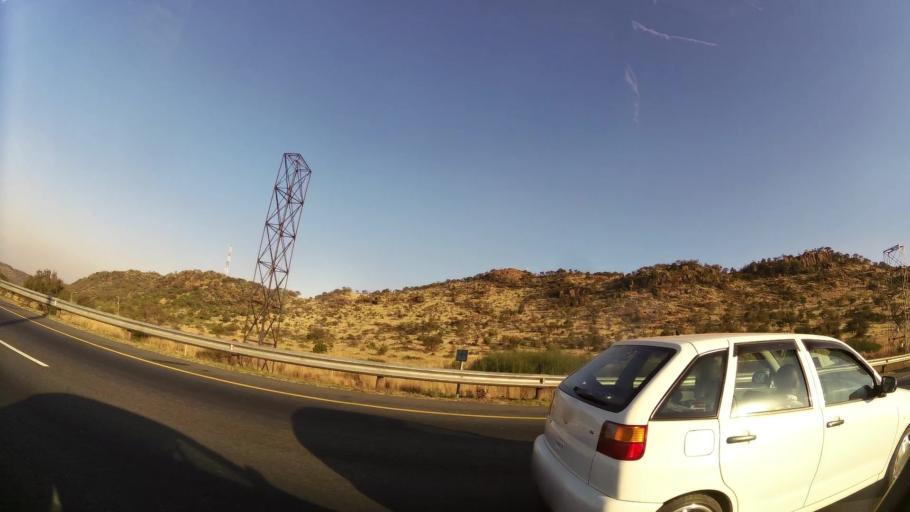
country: ZA
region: Gauteng
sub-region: City of Johannesburg Metropolitan Municipality
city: Johannesburg
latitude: -26.2664
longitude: 28.0742
